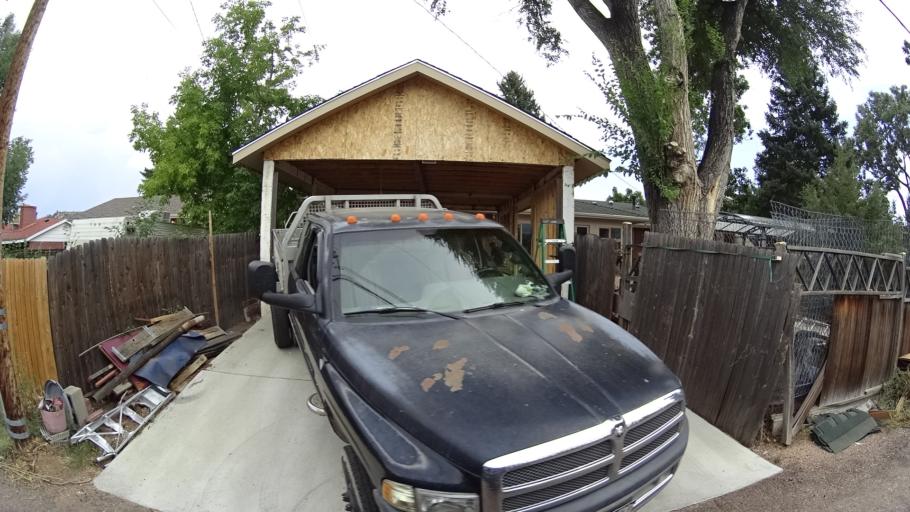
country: US
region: Colorado
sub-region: El Paso County
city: Colorado Springs
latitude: 38.8652
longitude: -104.7867
